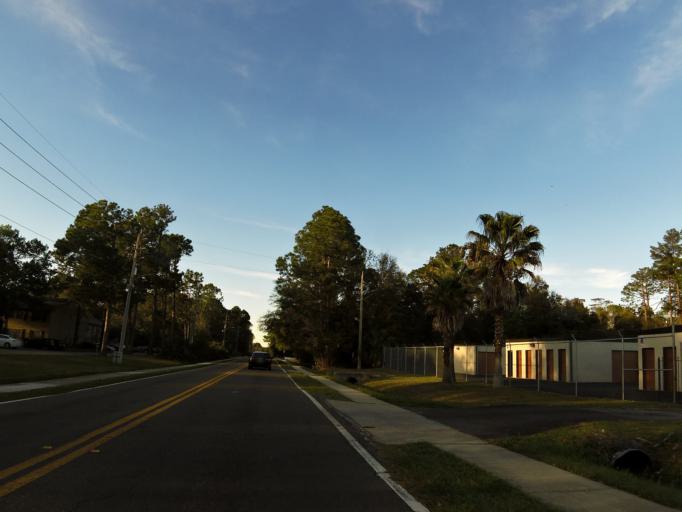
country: US
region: Florida
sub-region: Duval County
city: Jacksonville
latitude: 30.4312
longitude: -81.6716
